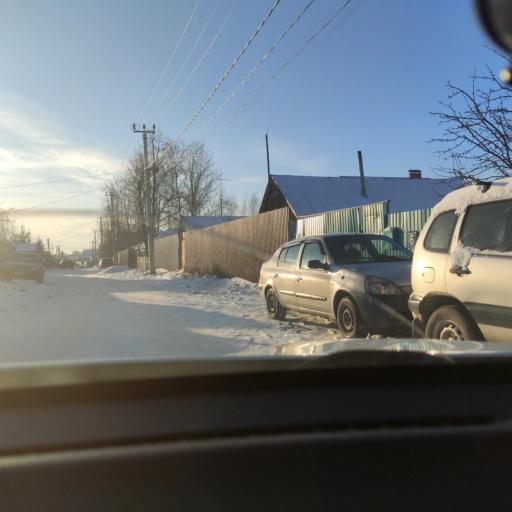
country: RU
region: Tatarstan
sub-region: Gorod Kazan'
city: Kazan
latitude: 55.7278
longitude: 49.1403
